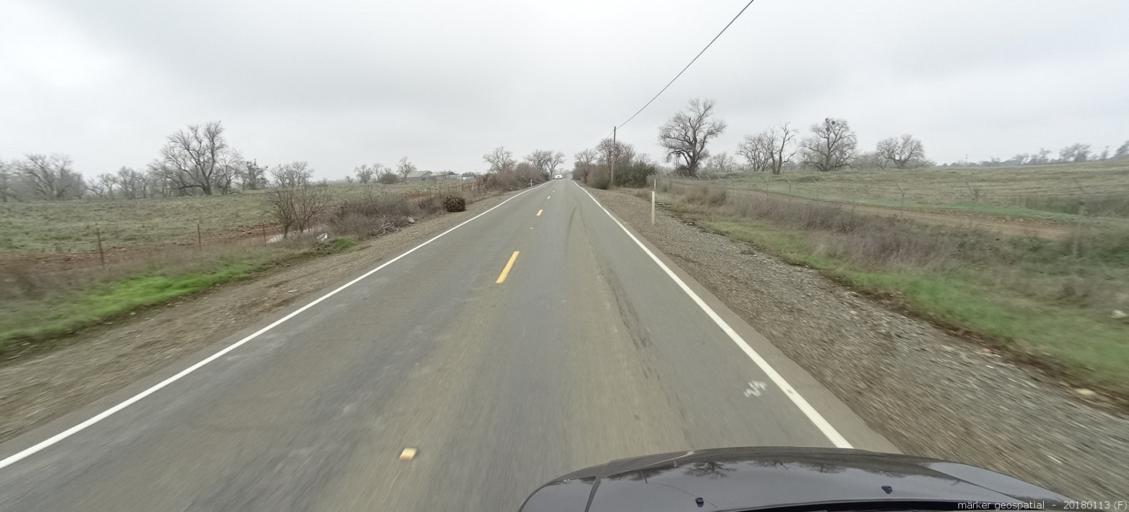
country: US
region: California
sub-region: Sacramento County
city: Gold River
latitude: 38.5927
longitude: -121.2173
